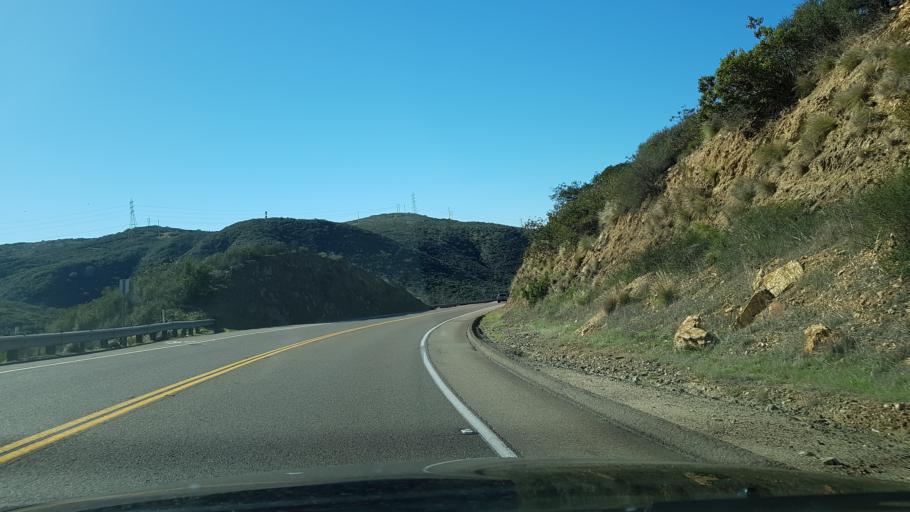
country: US
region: California
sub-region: San Diego County
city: Fairbanks Ranch
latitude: 33.0417
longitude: -117.1343
